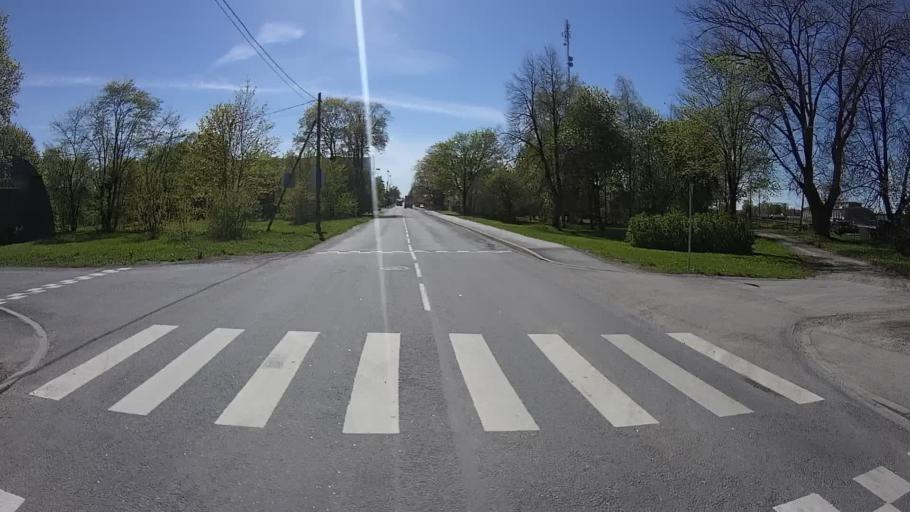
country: EE
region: Laeaene-Virumaa
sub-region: Tapa vald
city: Tapa
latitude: 59.2647
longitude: 25.9587
